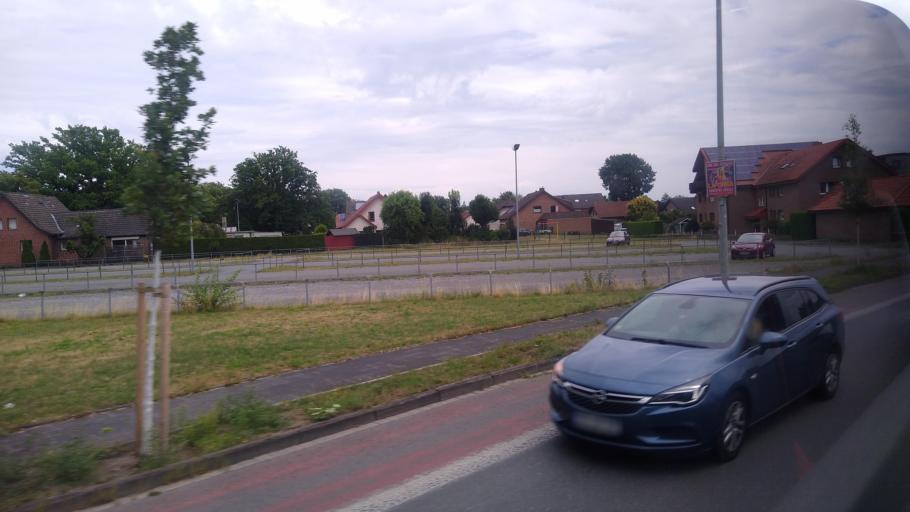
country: DE
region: North Rhine-Westphalia
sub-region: Regierungsbezirk Detmold
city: Hovelhof
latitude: 51.8271
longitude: 8.6501
